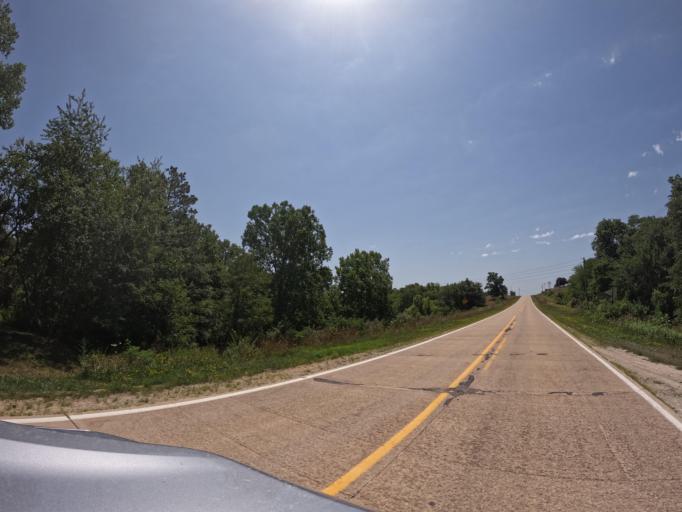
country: US
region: Iowa
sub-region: Henry County
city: Mount Pleasant
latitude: 40.9383
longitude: -91.5545
